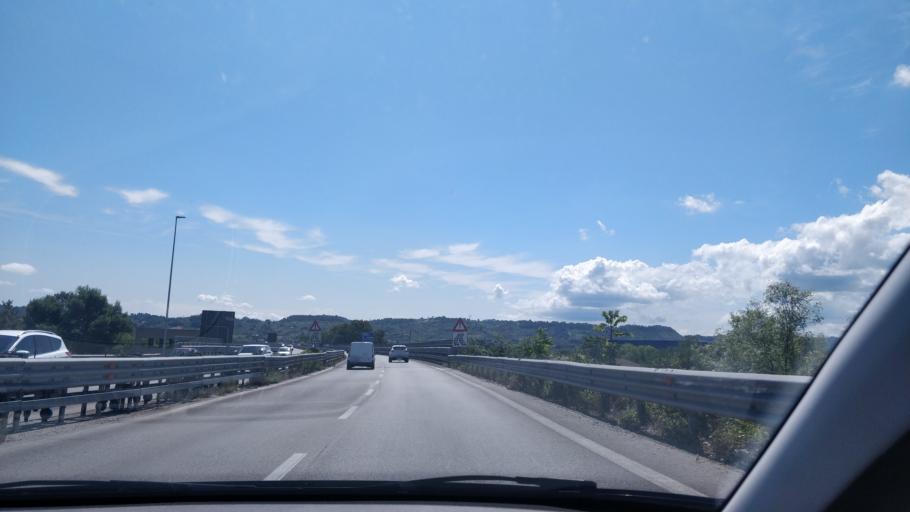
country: IT
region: Abruzzo
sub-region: Provincia di Pescara
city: Villa Raspa
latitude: 42.4502
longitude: 14.1815
